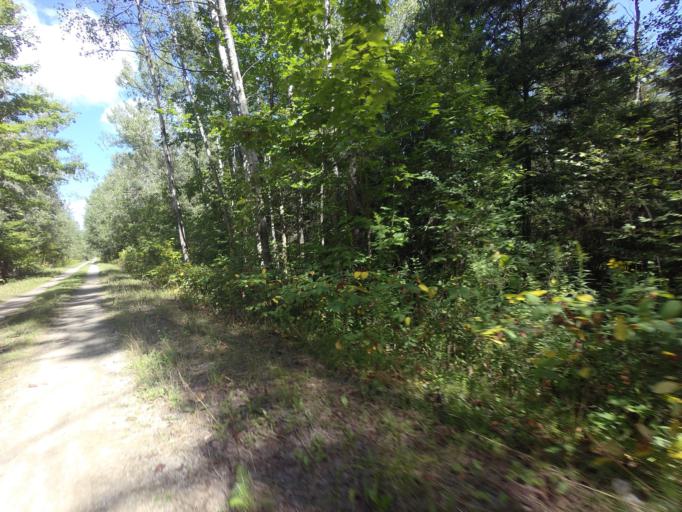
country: CA
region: Ontario
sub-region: Wellington County
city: Guelph
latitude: 43.7517
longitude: -80.3198
